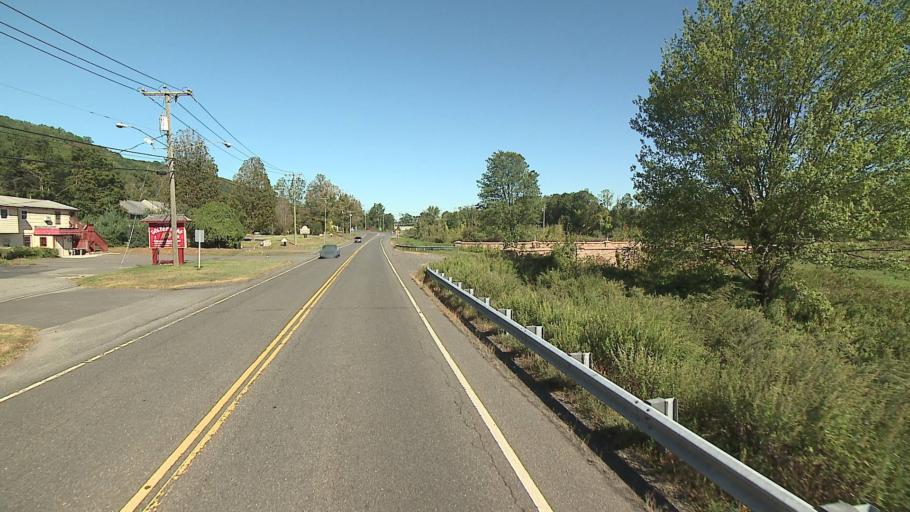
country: US
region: Connecticut
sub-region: Litchfield County
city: New Milford
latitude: 41.4953
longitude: -73.4170
